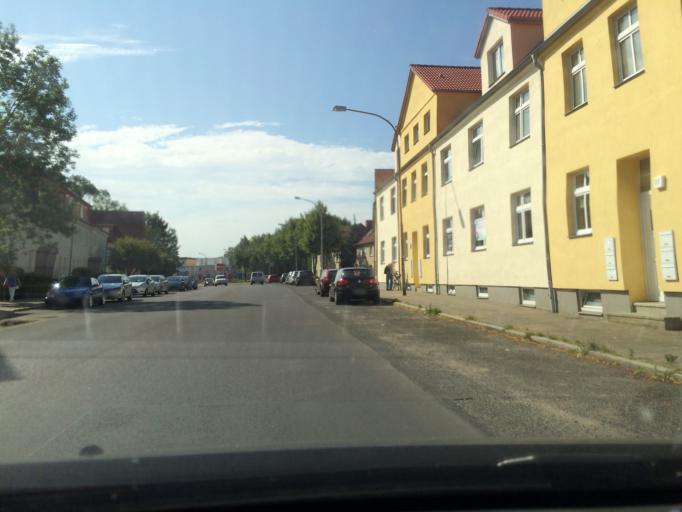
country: DE
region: Mecklenburg-Vorpommern
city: Stralsund
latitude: 54.3043
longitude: 13.0912
